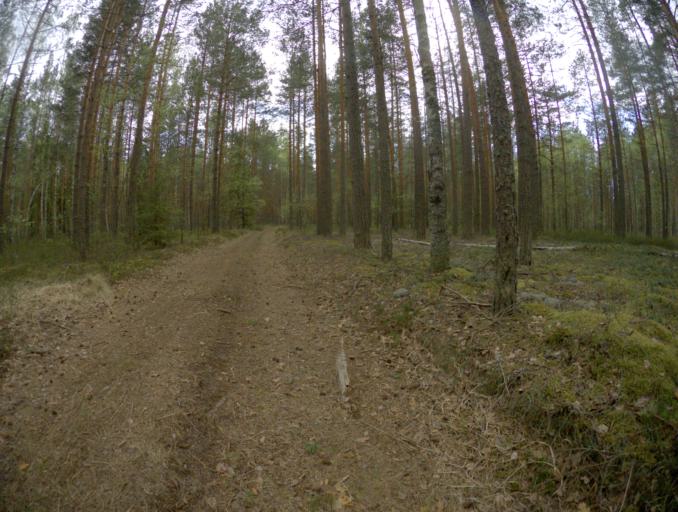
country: RU
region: Vladimir
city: Golovino
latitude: 55.8970
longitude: 40.3883
